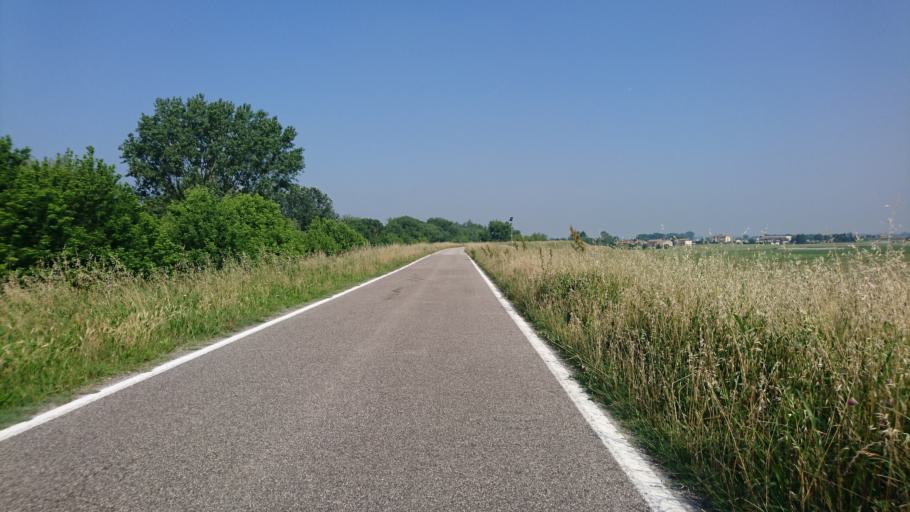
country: IT
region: Lombardy
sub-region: Provincia di Mantova
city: Carbonara di Po
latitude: 45.0527
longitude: 11.2263
